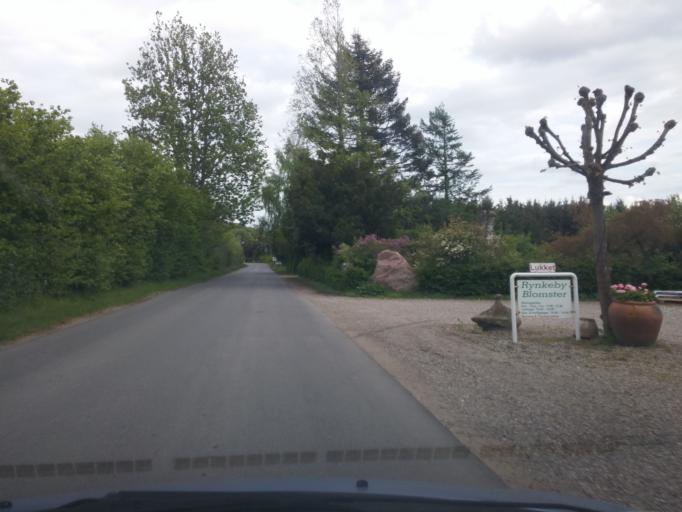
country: DK
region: South Denmark
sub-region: Kerteminde Kommune
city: Langeskov
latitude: 55.3979
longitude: 10.5984
